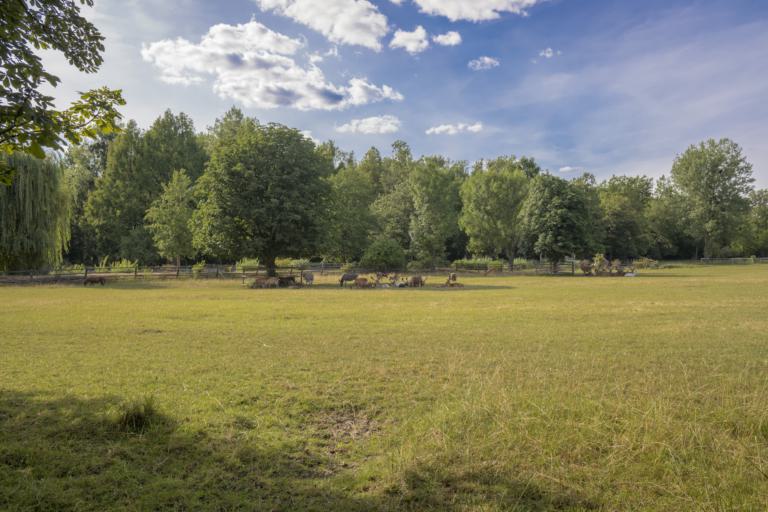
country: DE
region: Bavaria
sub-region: Upper Franconia
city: Weitramsdorf
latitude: 50.2293
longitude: 10.8614
